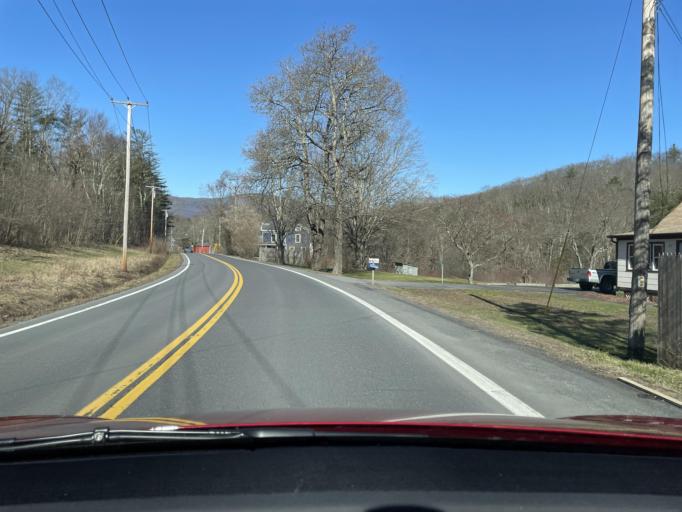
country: US
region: New York
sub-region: Ulster County
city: Saugerties
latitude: 42.0816
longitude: -73.9964
